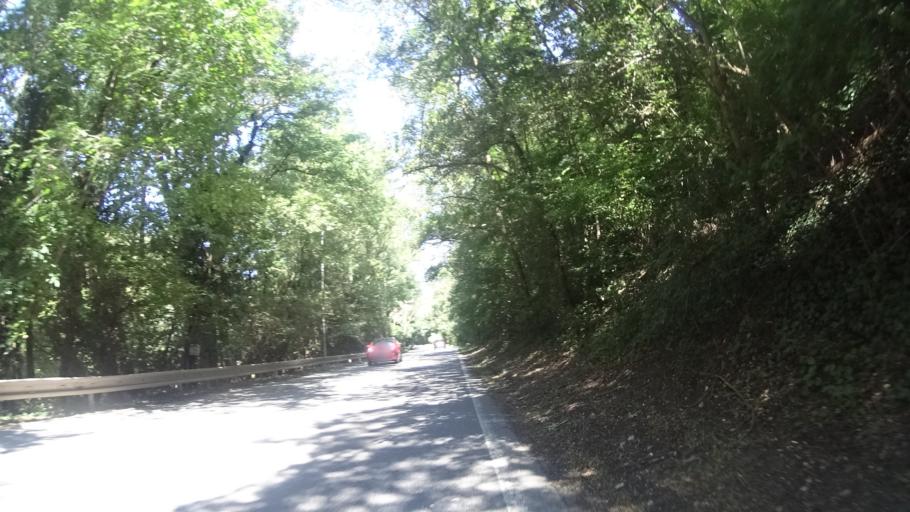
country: AT
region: Lower Austria
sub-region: Politischer Bezirk Bruck an der Leitha
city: Wolfsthal
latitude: 48.1555
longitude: 17.0180
